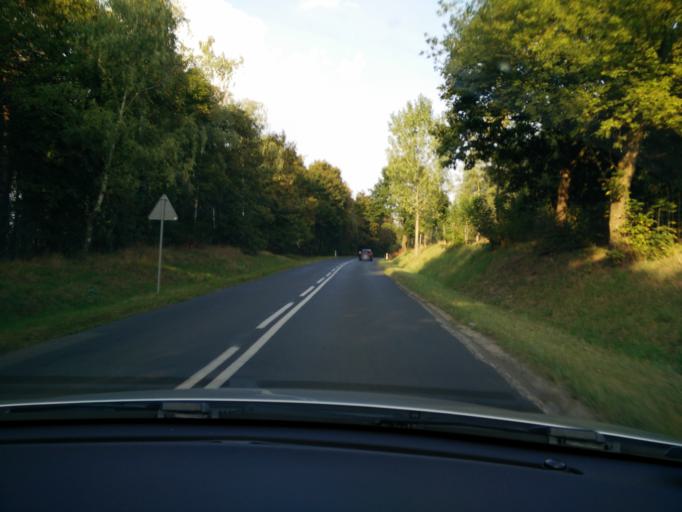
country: PL
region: Greater Poland Voivodeship
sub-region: Powiat wrzesinski
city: Miloslaw
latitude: 52.2790
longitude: 17.4771
